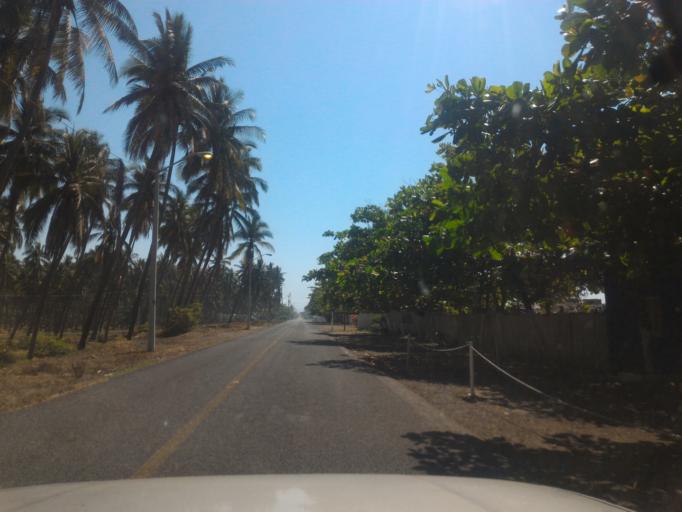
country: MX
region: Colima
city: Armeria
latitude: 18.8447
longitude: -103.9499
